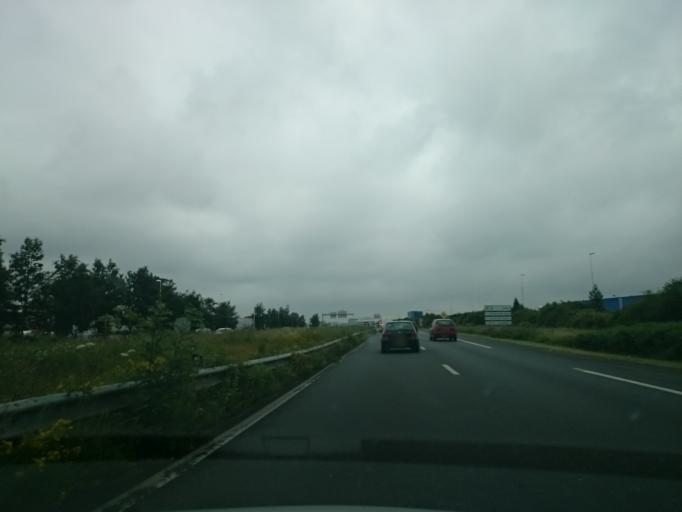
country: FR
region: Pays de la Loire
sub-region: Departement de la Loire-Atlantique
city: Saint-Herblain
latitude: 47.2309
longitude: -1.6433
